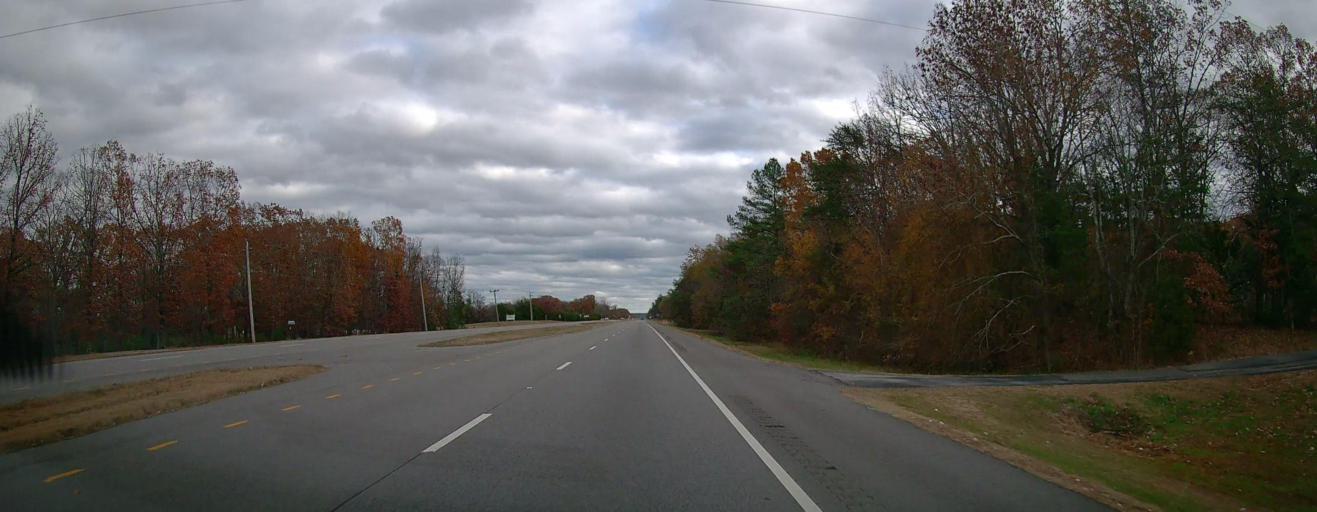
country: US
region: Alabama
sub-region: Colbert County
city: Muscle Shoals
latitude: 34.6663
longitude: -87.5539
